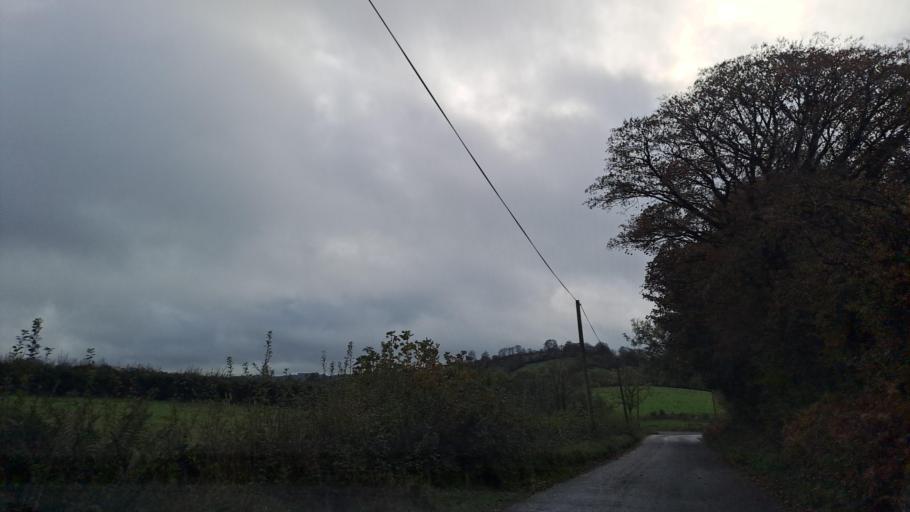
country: IE
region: Ulster
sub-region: An Cabhan
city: Bailieborough
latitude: 53.9454
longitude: -6.9800
